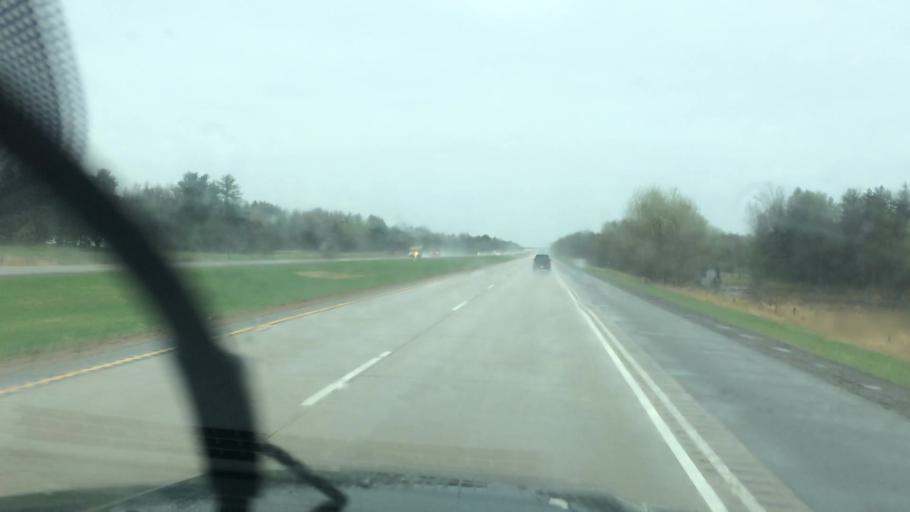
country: US
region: Wisconsin
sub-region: Portage County
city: Stevens Point
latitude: 44.6122
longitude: -89.6239
